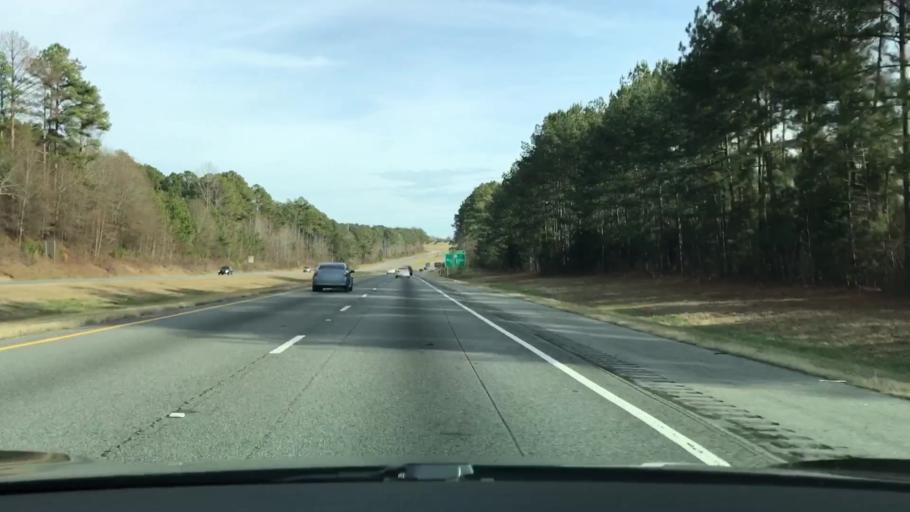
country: US
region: Georgia
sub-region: Walton County
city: Social Circle
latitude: 33.6111
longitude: -83.7144
